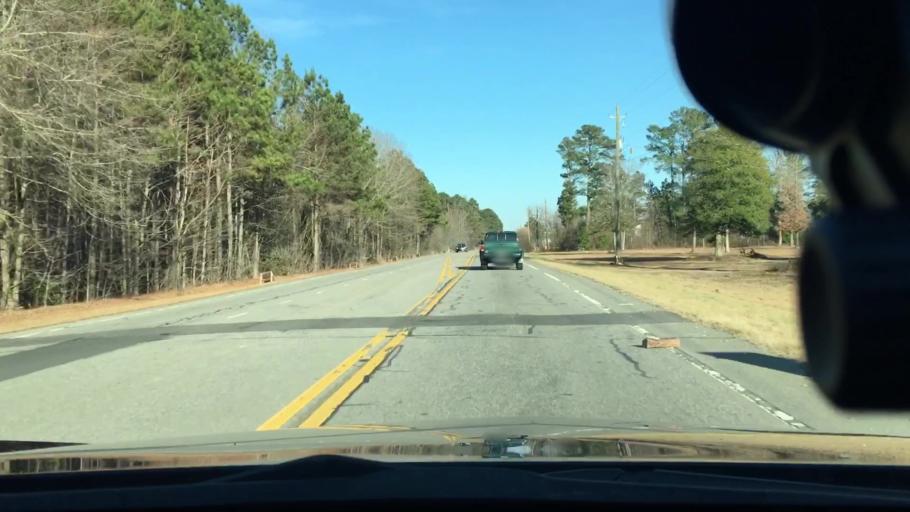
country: US
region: North Carolina
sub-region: Moore County
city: Carthage
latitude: 35.3782
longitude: -79.2884
